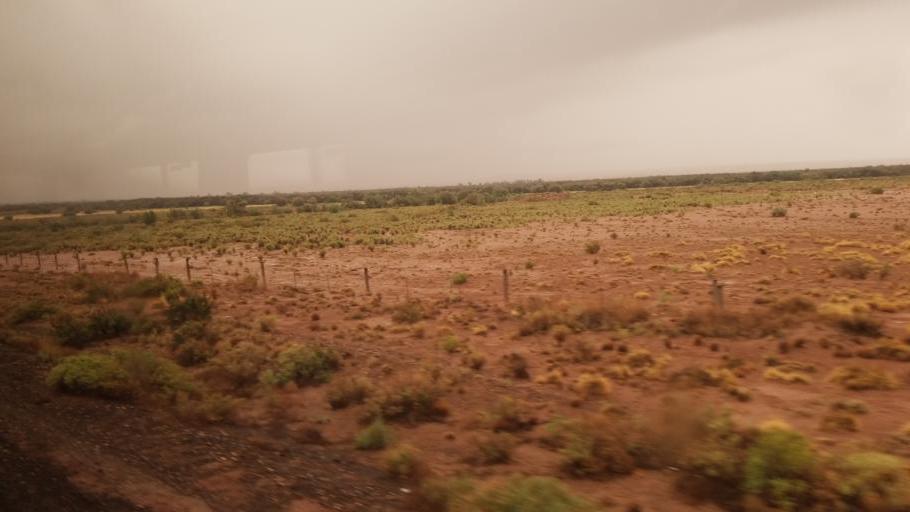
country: US
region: Arizona
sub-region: Navajo County
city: Joseph City
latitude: 34.9674
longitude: -110.4819
